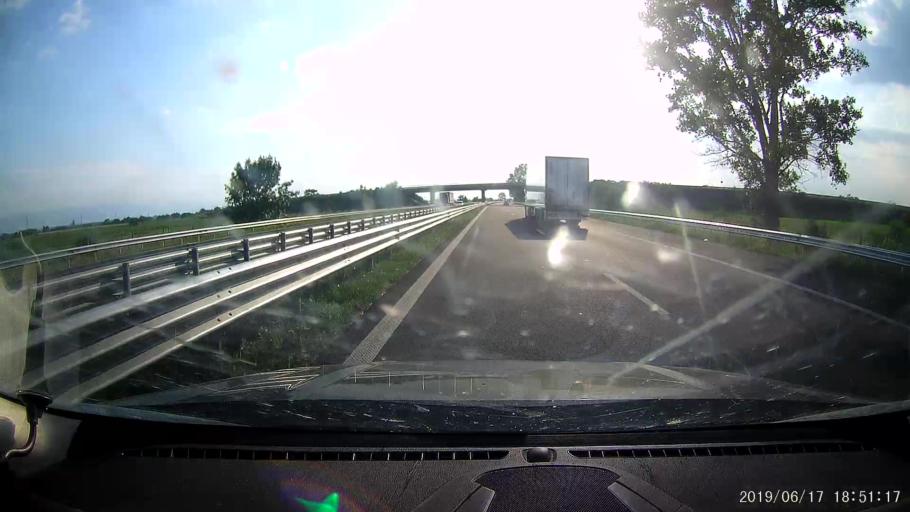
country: BG
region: Plovdiv
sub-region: Obshtina Rakovski
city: Rakovski
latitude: 42.2136
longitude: 24.9763
